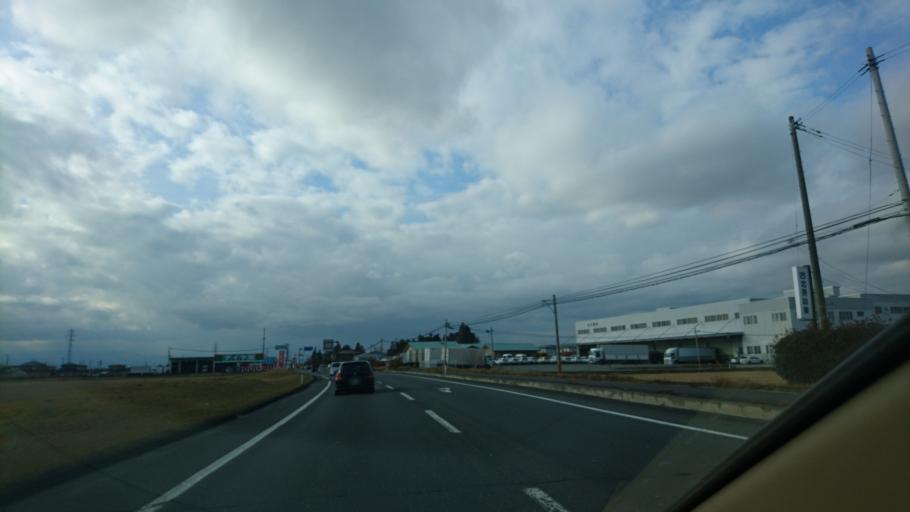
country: JP
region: Miyagi
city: Kogota
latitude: 38.5596
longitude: 141.0328
